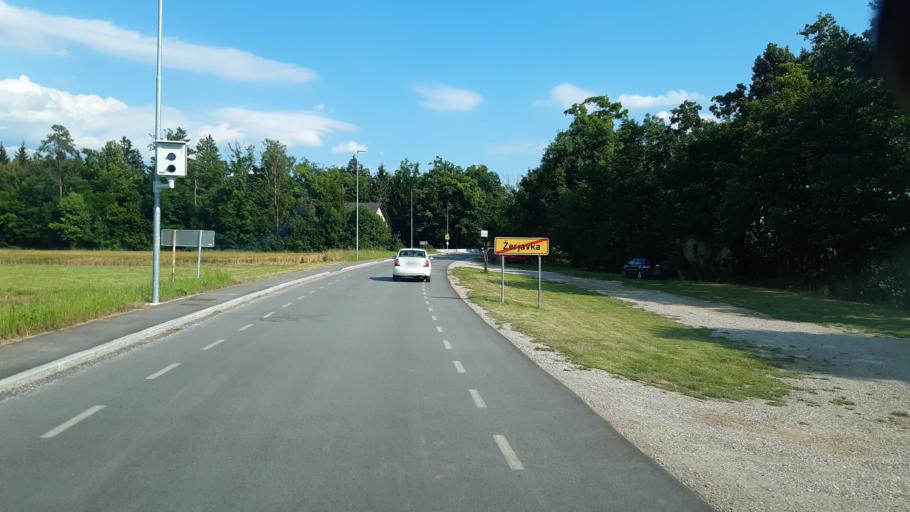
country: SI
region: Sencur
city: Hrastje
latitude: 46.2017
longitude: 14.4068
